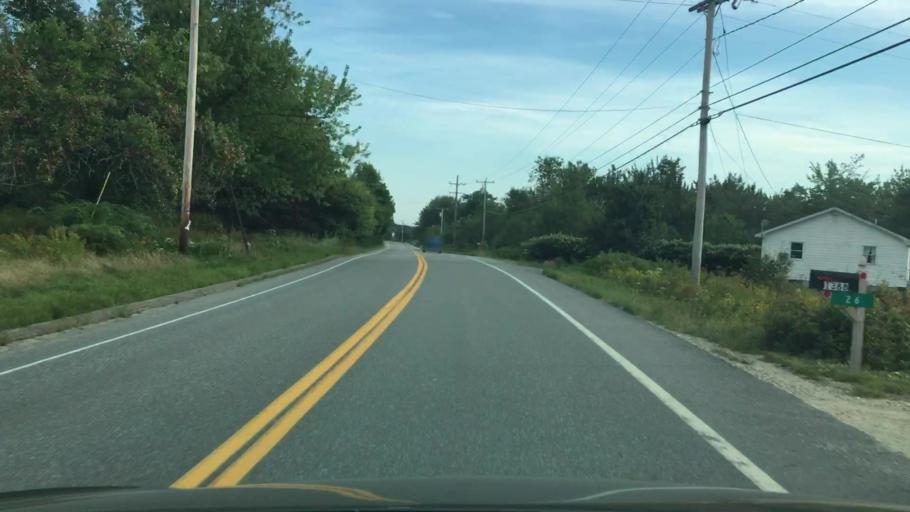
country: US
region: Maine
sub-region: Hancock County
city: Penobscot
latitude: 44.4705
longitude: -68.7817
